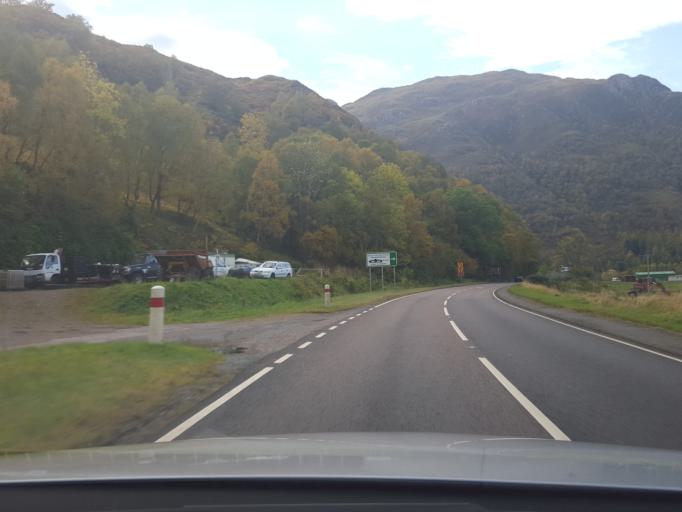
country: GB
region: Scotland
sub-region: Highland
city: Fort William
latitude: 57.2181
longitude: -5.4189
